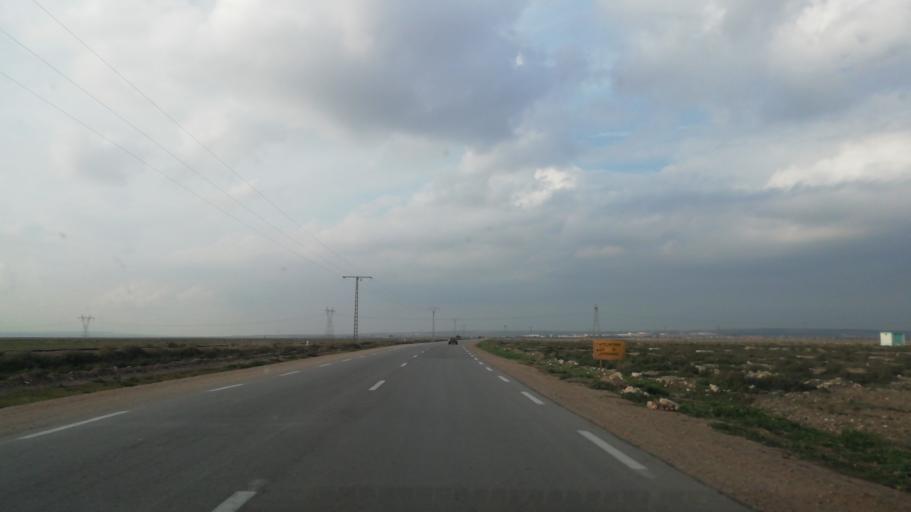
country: DZ
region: Mascara
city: Sig
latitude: 35.6984
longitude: -0.0236
